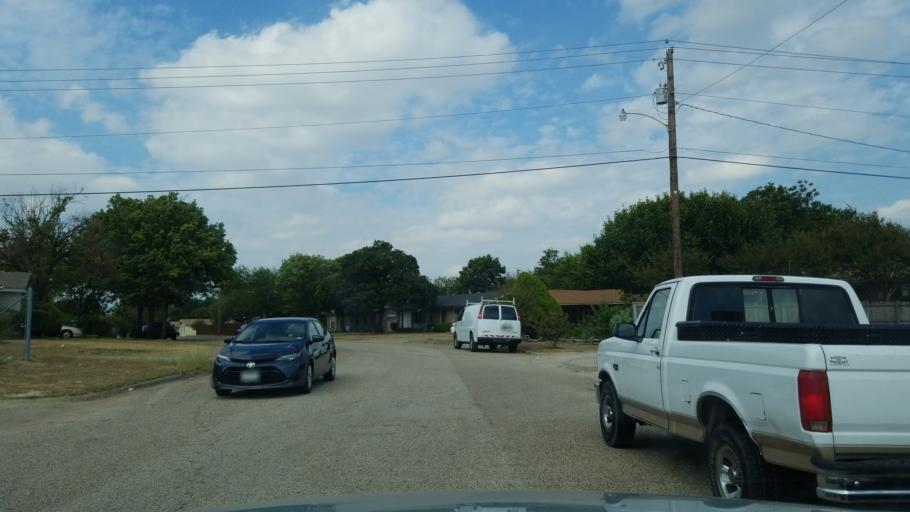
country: US
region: Texas
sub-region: Dallas County
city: Garland
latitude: 32.9100
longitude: -96.6869
